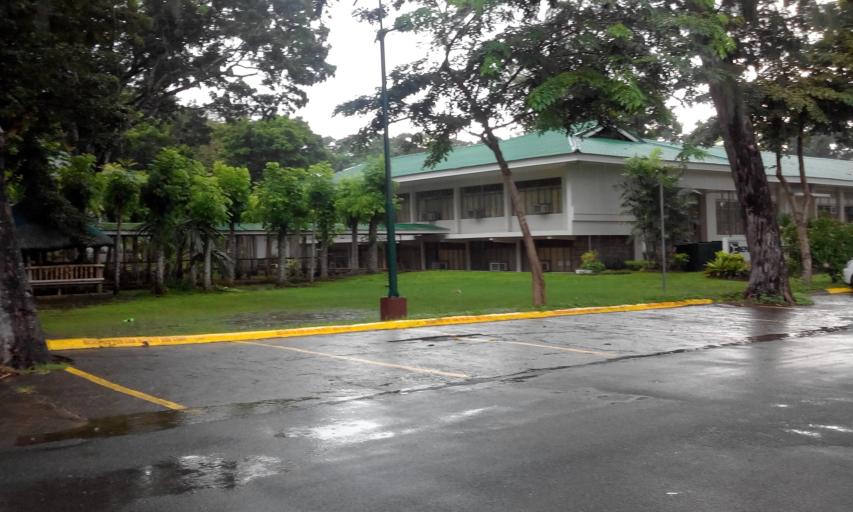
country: PH
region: Calabarzon
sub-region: Province of Laguna
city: Los Banos
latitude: 14.1673
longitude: 121.2422
